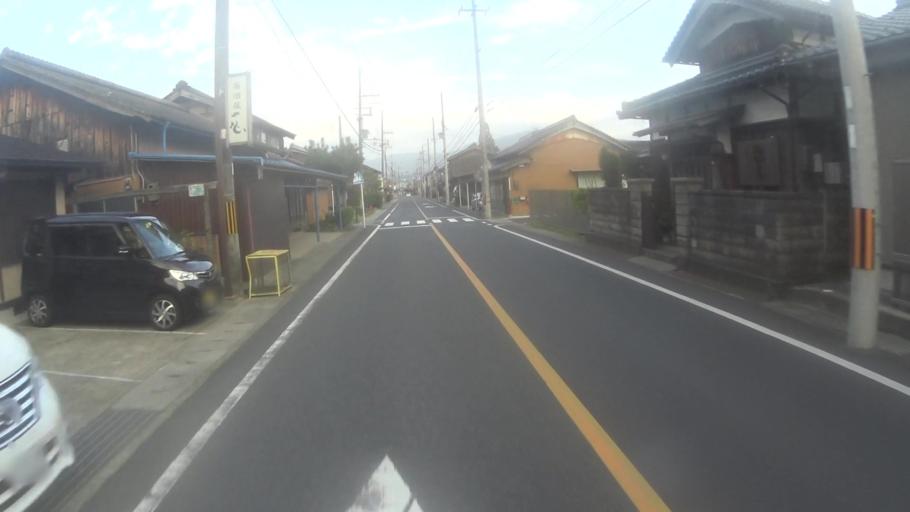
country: JP
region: Kyoto
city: Miyazu
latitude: 35.5299
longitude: 135.0948
